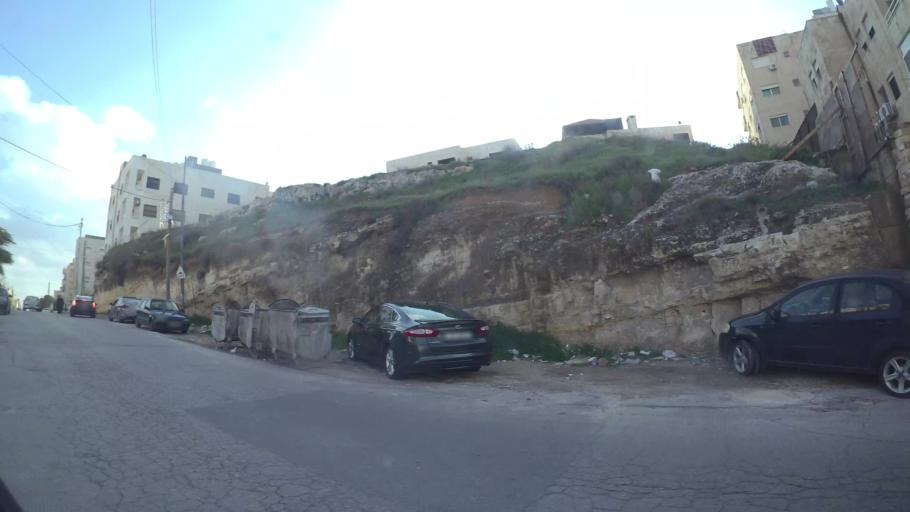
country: JO
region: Amman
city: Al Jubayhah
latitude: 31.9983
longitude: 35.8689
